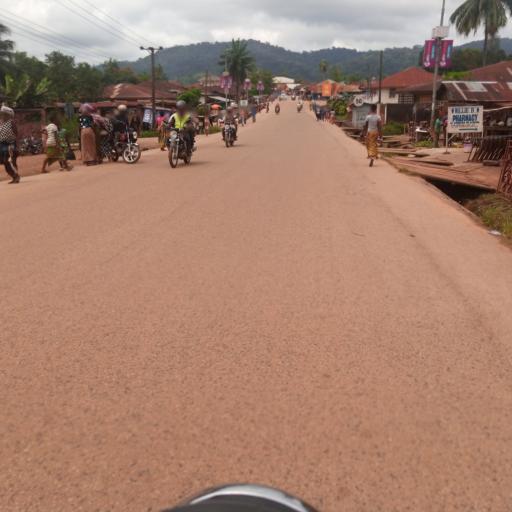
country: SL
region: Eastern Province
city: Kenema
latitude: 7.8761
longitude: -11.1855
